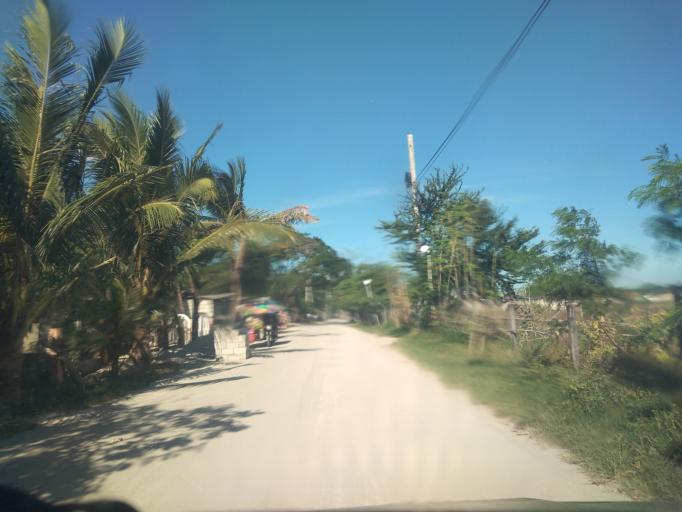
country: PH
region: Central Luzon
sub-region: Province of Pampanga
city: Calibutbut
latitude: 15.0907
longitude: 120.5977
